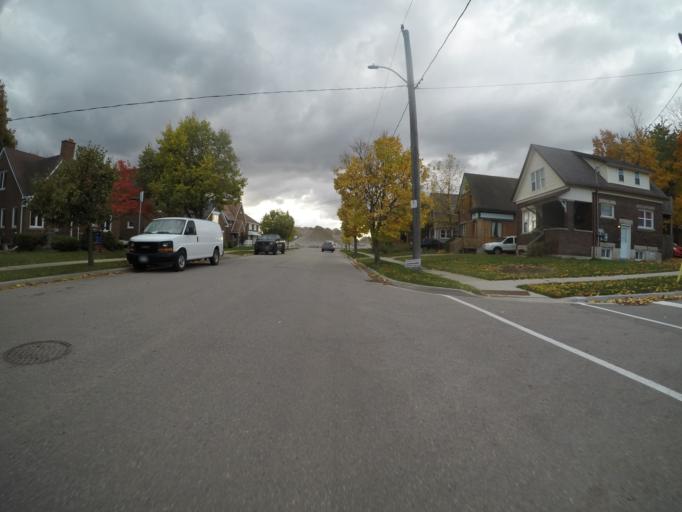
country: CA
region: Ontario
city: Kitchener
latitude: 43.4396
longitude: -80.4802
